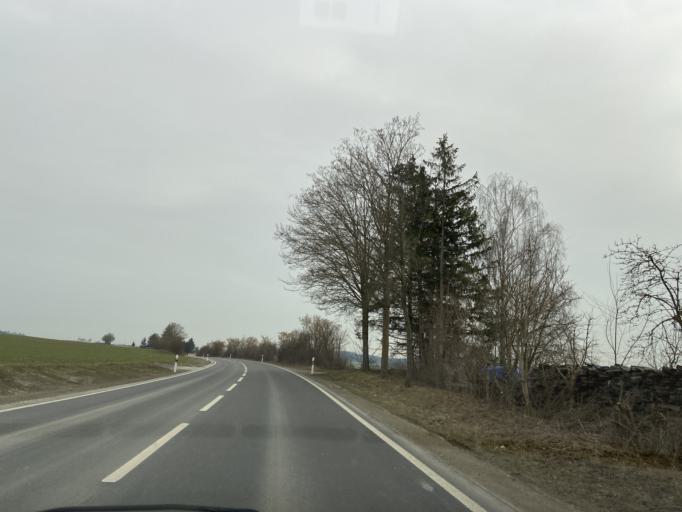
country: DE
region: Baden-Wuerttemberg
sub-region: Tuebingen Region
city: Konigseggwald
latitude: 47.9461
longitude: 9.4072
